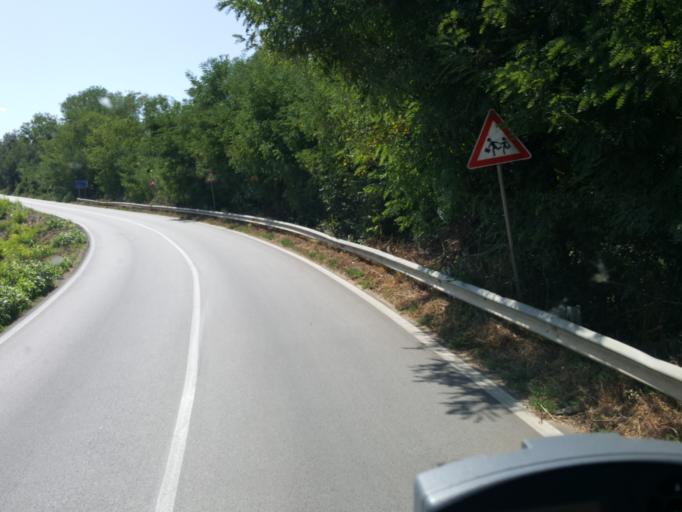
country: IT
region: Latium
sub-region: Provincia di Latina
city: Priverno
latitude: 41.4396
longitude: 13.1948
